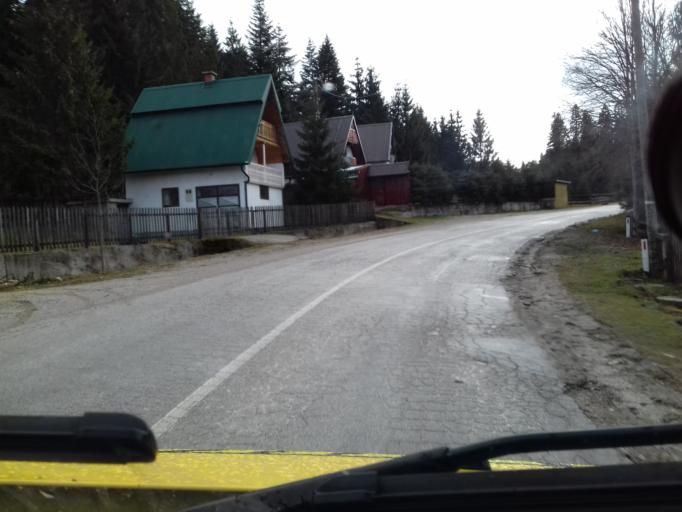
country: BA
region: Federation of Bosnia and Herzegovina
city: Turbe
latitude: 44.3080
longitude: 17.4912
